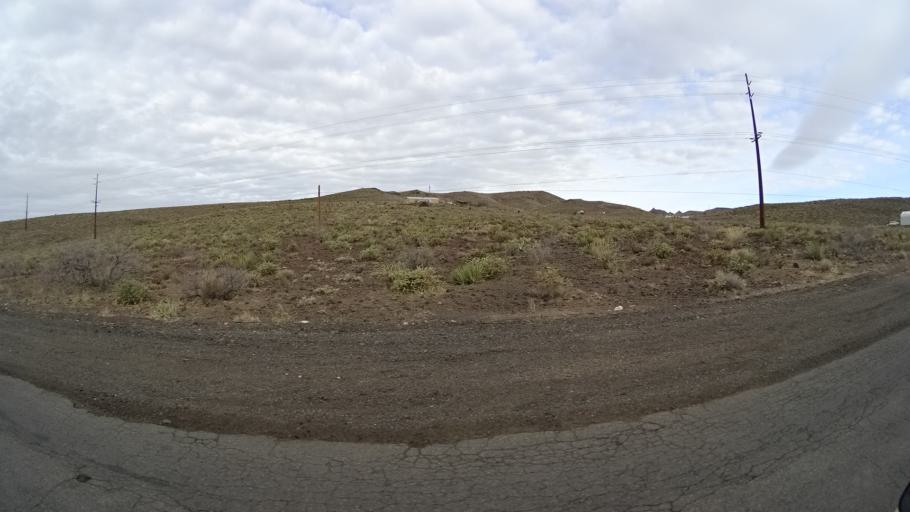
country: US
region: Arizona
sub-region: Mohave County
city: Kingman
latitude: 35.2133
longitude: -114.0775
